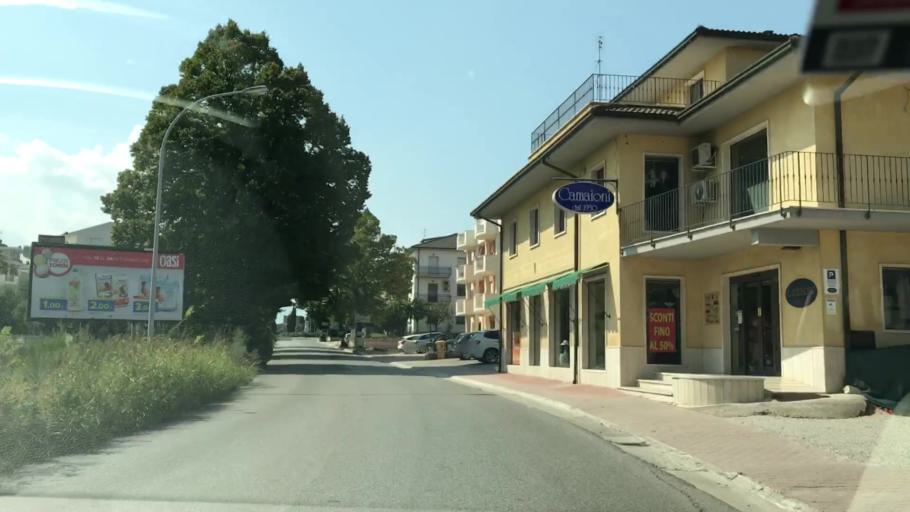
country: IT
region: The Marches
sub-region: Provincia di Ascoli Piceno
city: Pagliare
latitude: 42.8744
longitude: 13.7688
